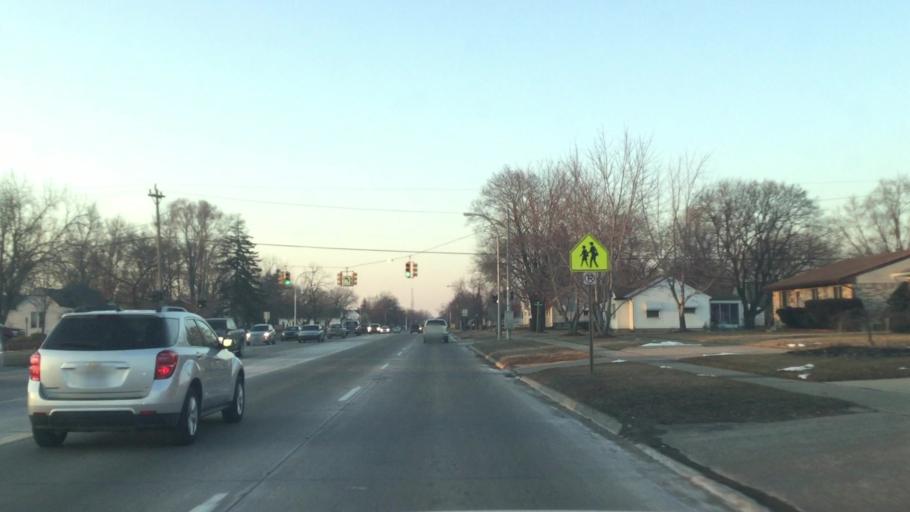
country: US
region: Michigan
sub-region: Wayne County
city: Garden City
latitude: 42.3272
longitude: -83.3504
